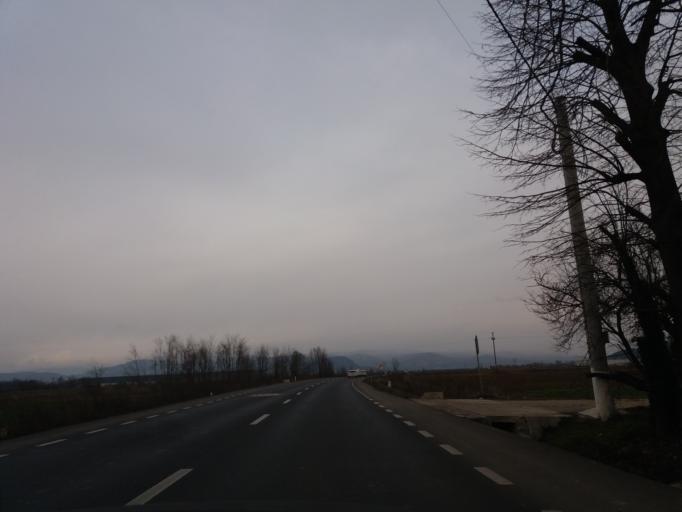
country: RO
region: Hunedoara
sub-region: Comuna Bacia
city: Bacia
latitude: 45.8071
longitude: 23.0144
